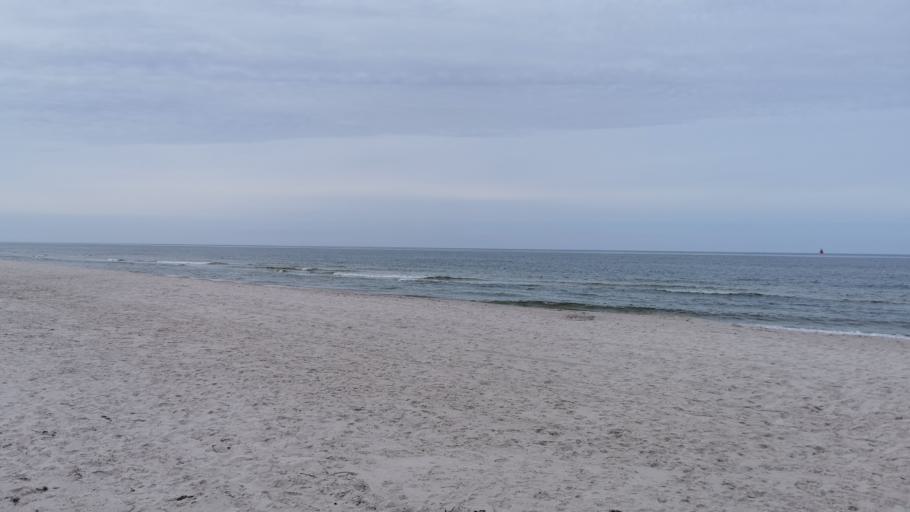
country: PL
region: Pomeranian Voivodeship
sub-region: Powiat leborski
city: Leba
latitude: 54.7913
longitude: 17.7099
